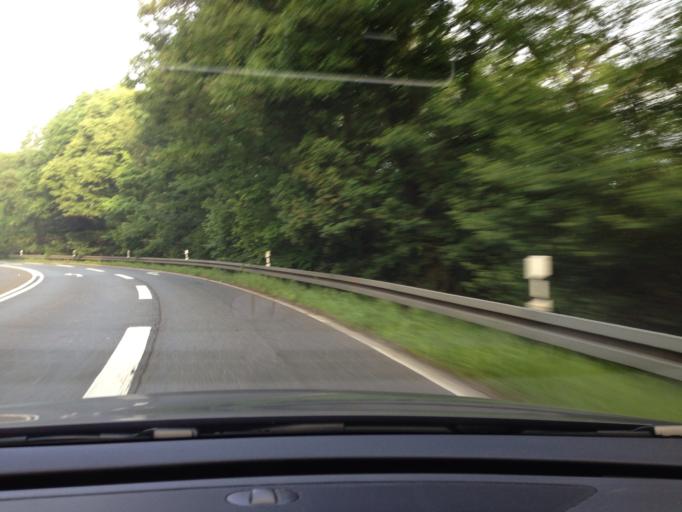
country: DE
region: North Rhine-Westphalia
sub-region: Regierungsbezirk Dusseldorf
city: Hilden
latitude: 51.1935
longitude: 6.9165
